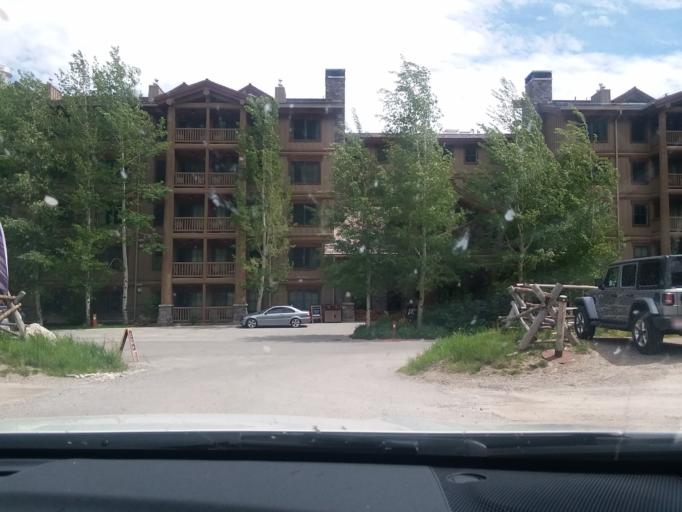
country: US
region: Wyoming
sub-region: Teton County
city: Moose Wilson Road
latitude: 43.5871
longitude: -110.8304
